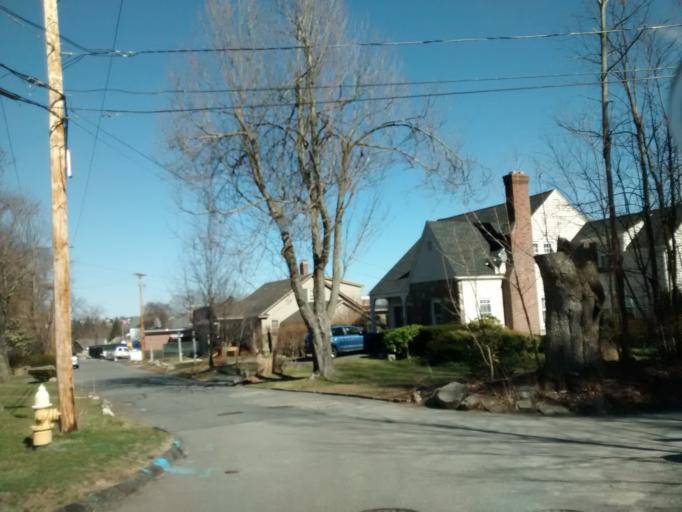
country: US
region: Massachusetts
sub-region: Worcester County
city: Worcester
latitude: 42.2951
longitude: -71.8233
